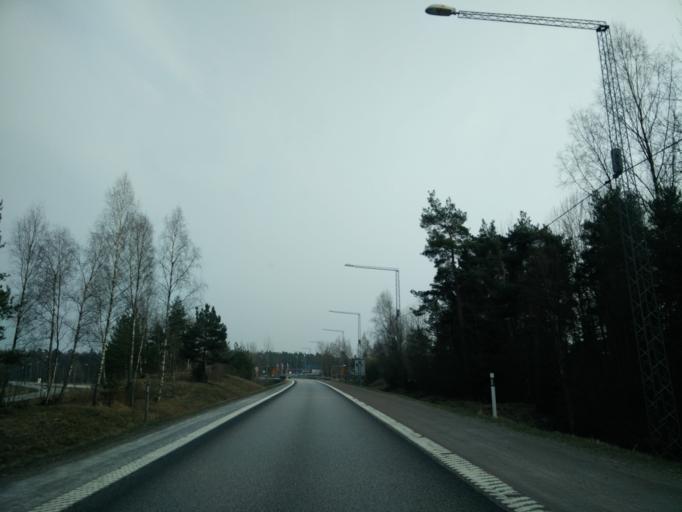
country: SE
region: Vaermland
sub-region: Hammaro Kommun
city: Skoghall
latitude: 59.3809
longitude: 13.4267
